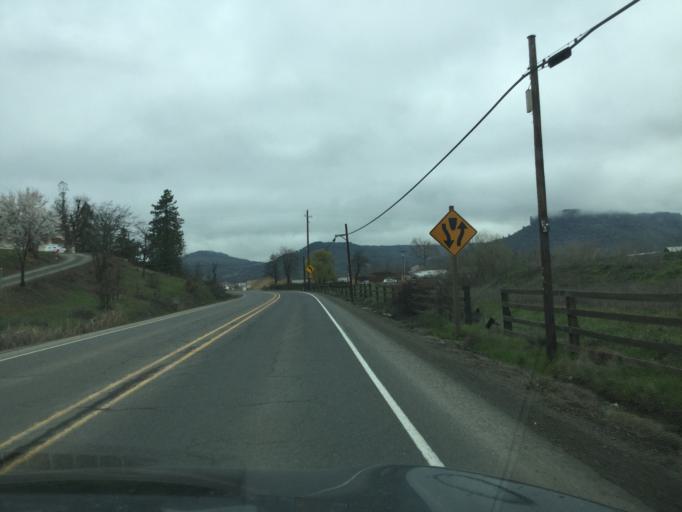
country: US
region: Oregon
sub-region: Jackson County
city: Central Point
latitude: 42.4174
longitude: -122.9522
